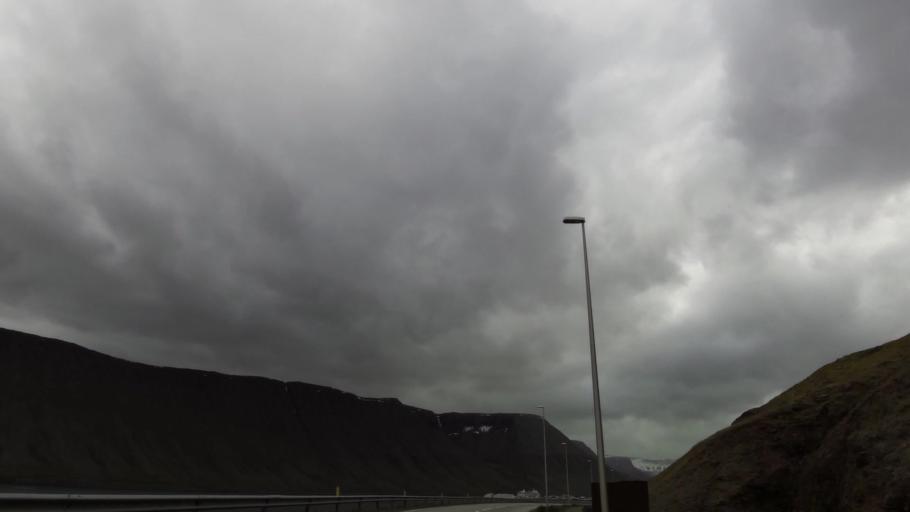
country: IS
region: Westfjords
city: Isafjoerdur
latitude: 66.0929
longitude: -23.1132
